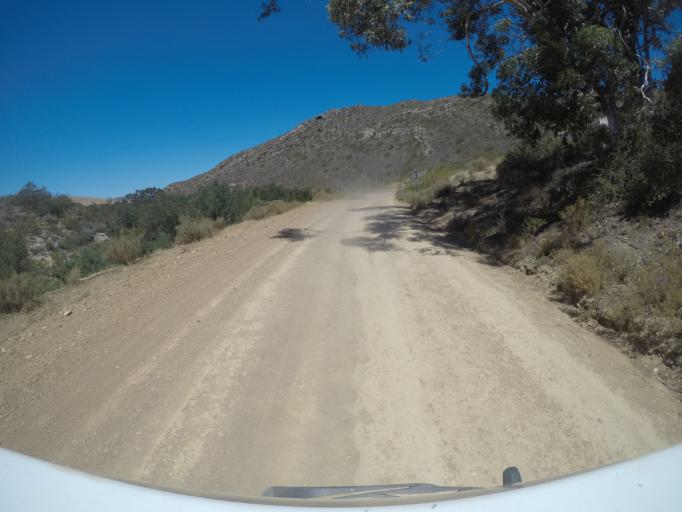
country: ZA
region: Western Cape
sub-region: Overberg District Municipality
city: Caledon
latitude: -34.1191
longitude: 19.2356
